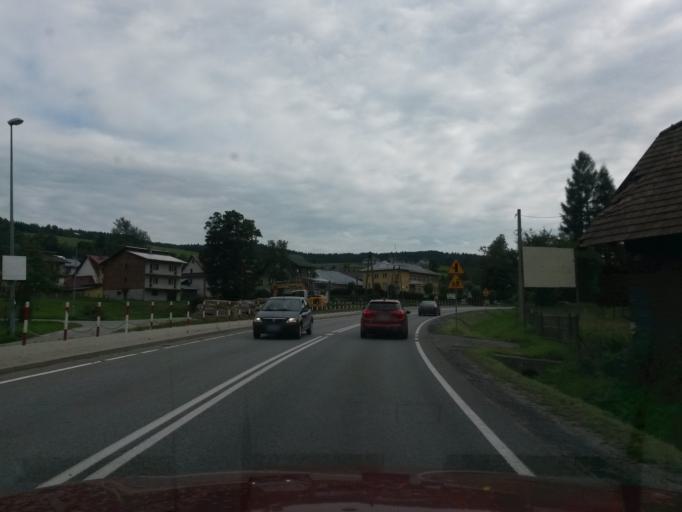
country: PL
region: Lesser Poland Voivodeship
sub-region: Powiat nowosadecki
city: Labowa
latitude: 49.4961
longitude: 20.9069
